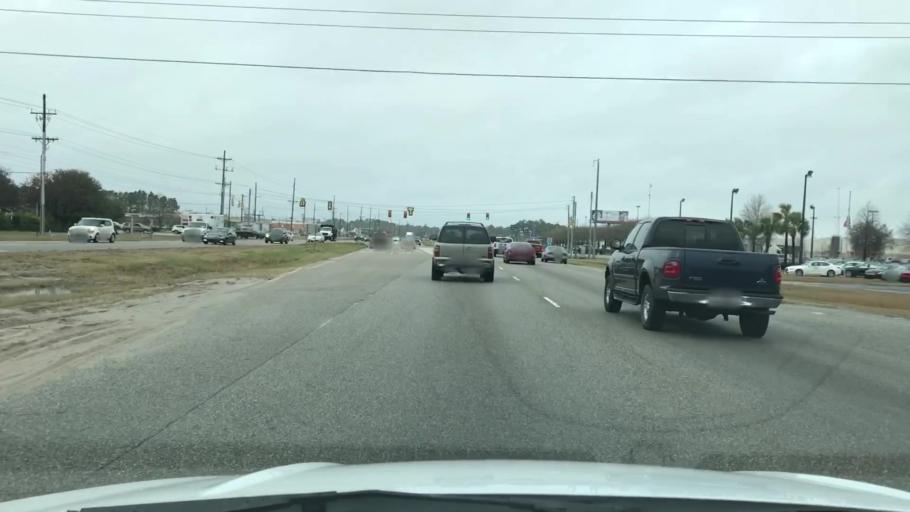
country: US
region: South Carolina
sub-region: Horry County
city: Red Hill
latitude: 33.7896
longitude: -78.9958
